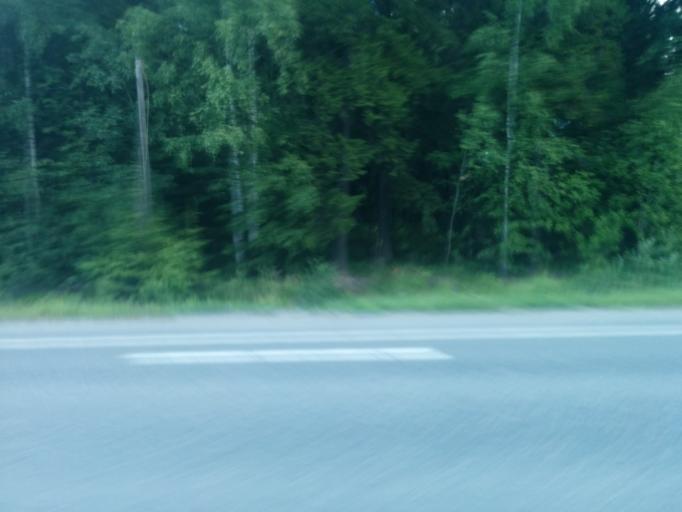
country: FI
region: Pirkanmaa
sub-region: Tampere
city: Kangasala
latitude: 61.5291
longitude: 23.9436
